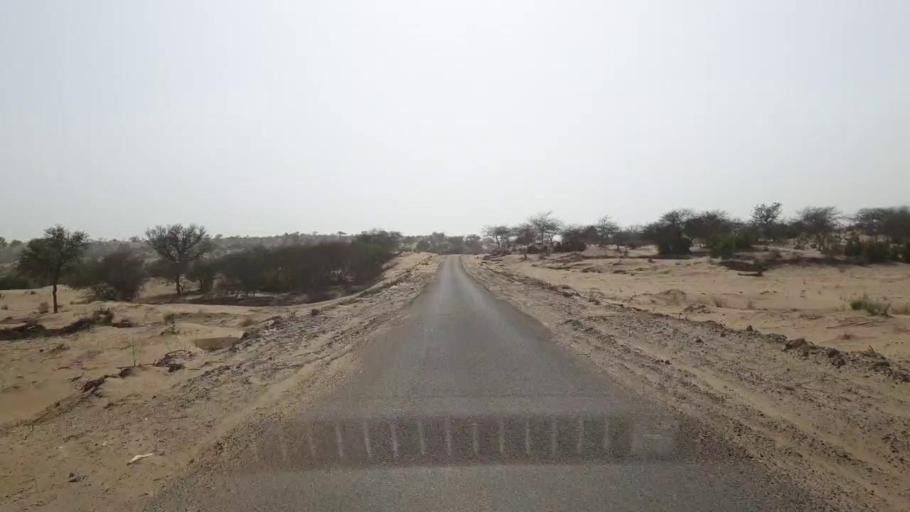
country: PK
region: Sindh
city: Mithi
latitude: 24.6186
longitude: 69.8851
